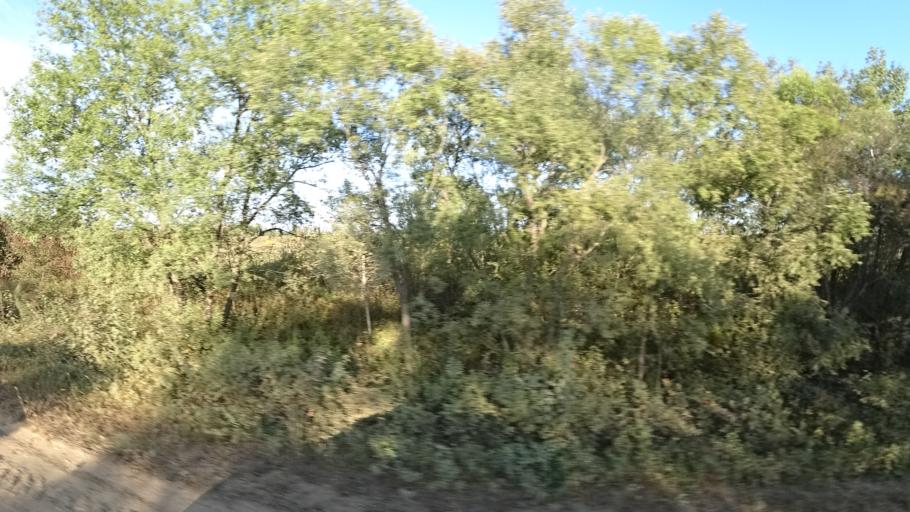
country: RU
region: Amur
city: Arkhara
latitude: 49.3668
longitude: 130.1361
